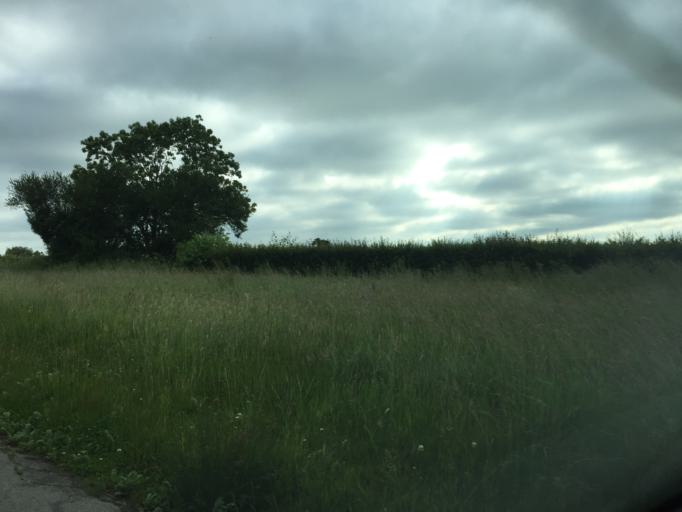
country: GB
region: England
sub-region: South Gloucestershire
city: Horton
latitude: 51.5683
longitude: -2.3553
